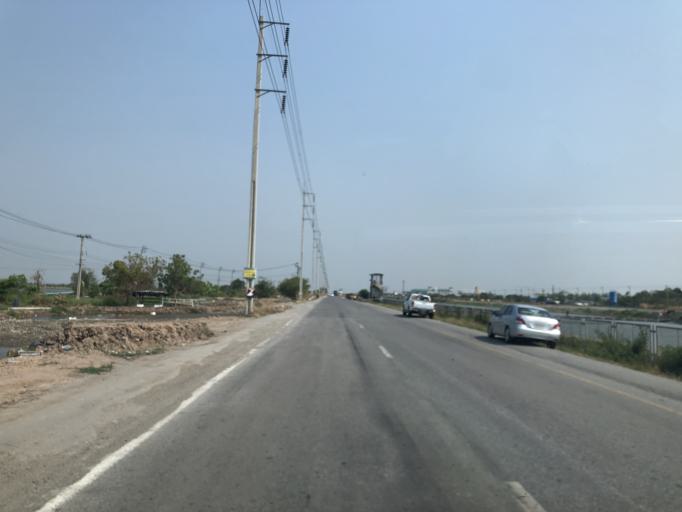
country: TH
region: Samut Prakan
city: Bang Bo District
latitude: 13.5129
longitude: 100.7454
